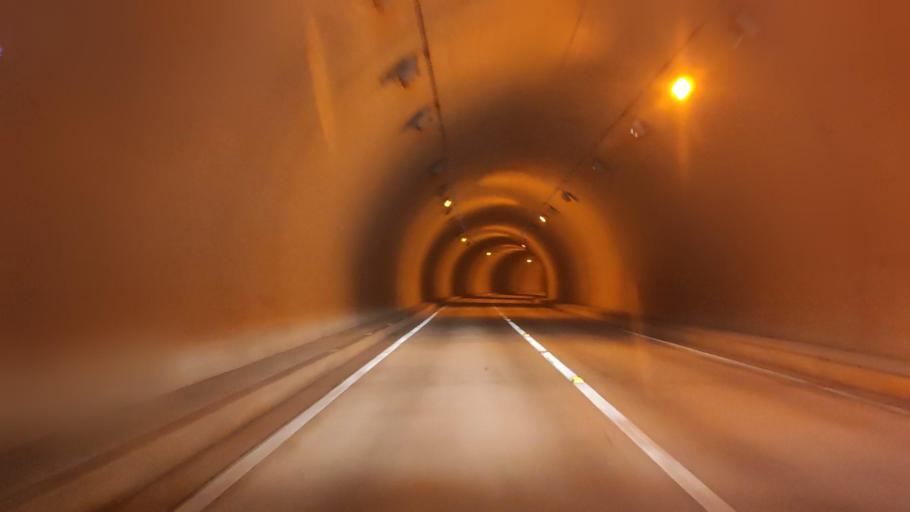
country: JP
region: Nagasaki
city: Shimabara
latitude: 32.7628
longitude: 130.2759
